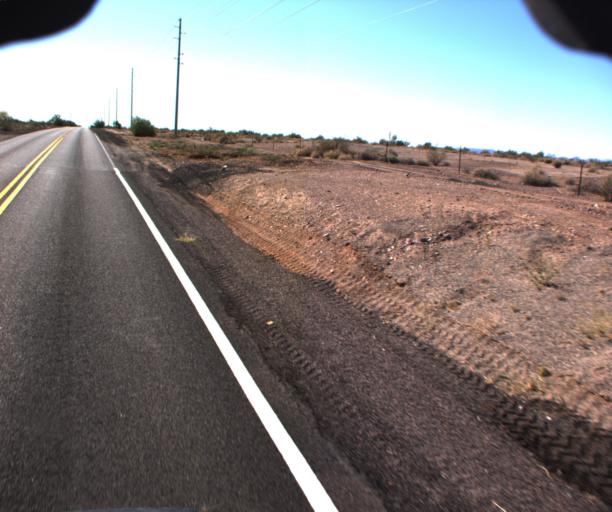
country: US
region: Arizona
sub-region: La Paz County
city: Quartzsite
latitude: 33.9071
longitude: -113.9824
